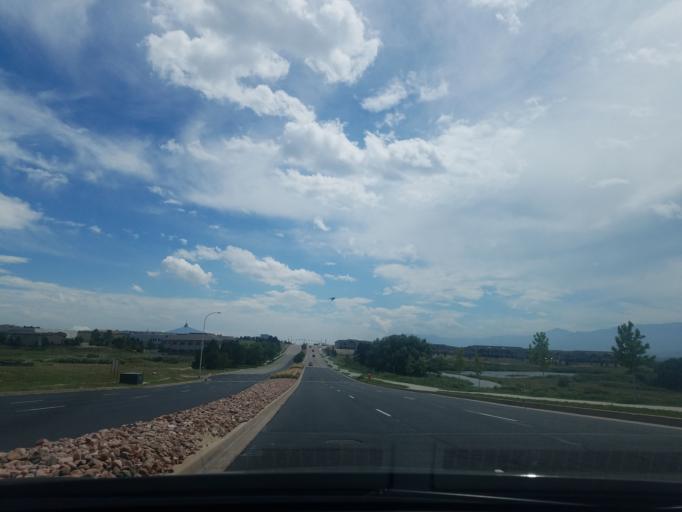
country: US
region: Colorado
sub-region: El Paso County
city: Gleneagle
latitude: 39.0009
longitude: -104.7980
